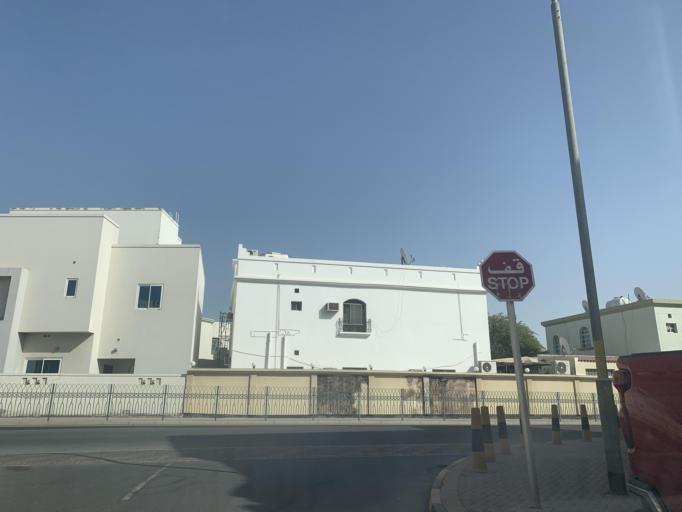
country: BH
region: Northern
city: Madinat `Isa
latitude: 26.1634
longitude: 50.5771
